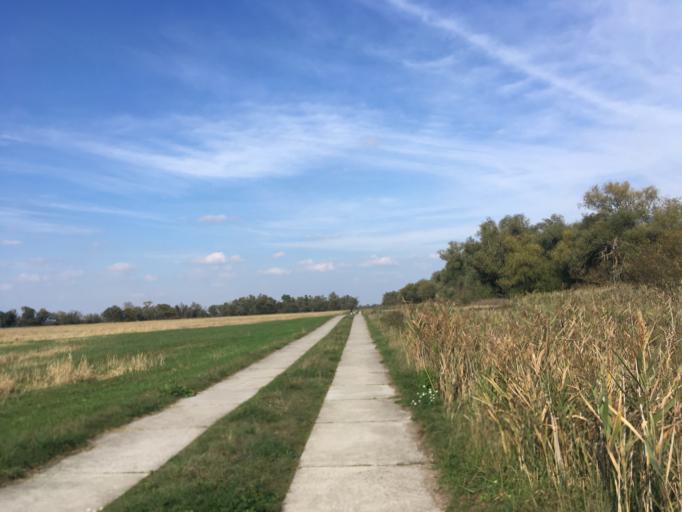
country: DE
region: Brandenburg
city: Schwedt (Oder)
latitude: 53.0191
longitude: 14.2750
